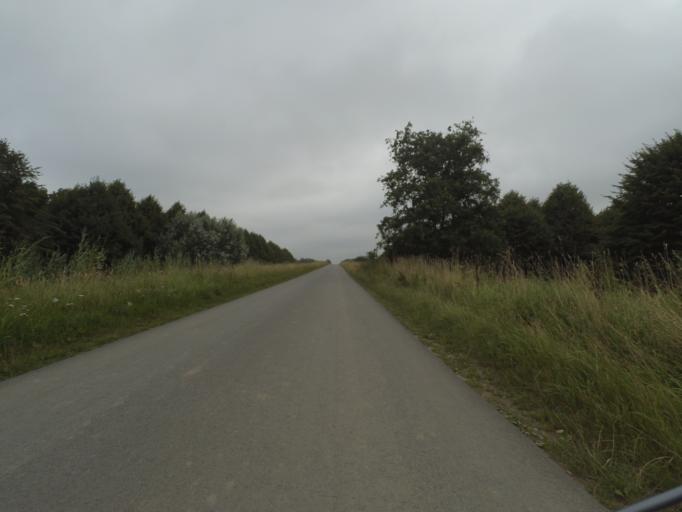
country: NL
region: Flevoland
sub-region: Gemeente Lelystad
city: Lelystad
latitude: 52.4710
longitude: 5.4524
